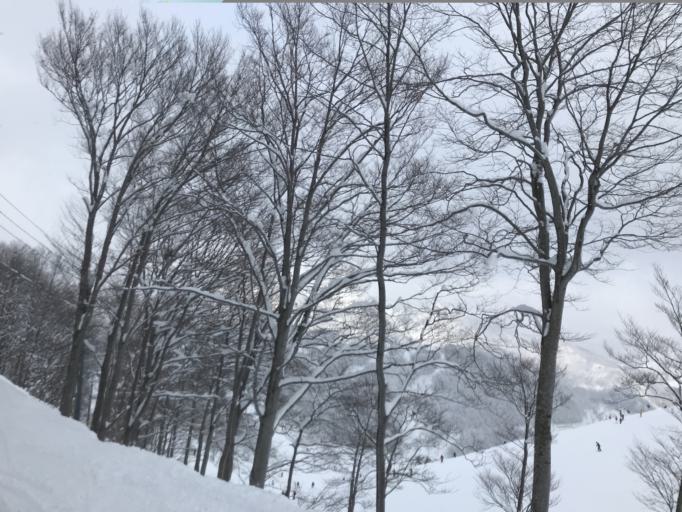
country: JP
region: Nagano
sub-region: Kitaazumi Gun
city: Hakuba
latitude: 36.7060
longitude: 137.8121
